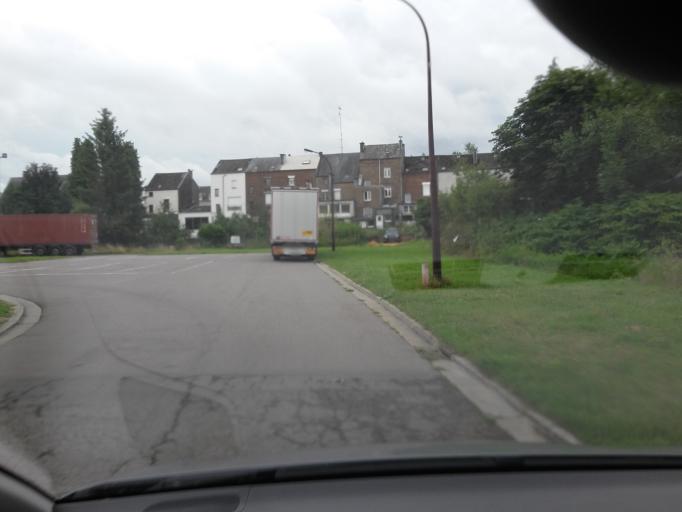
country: BE
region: Wallonia
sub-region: Province du Luxembourg
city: Arlon
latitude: 49.6790
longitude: 5.8010
